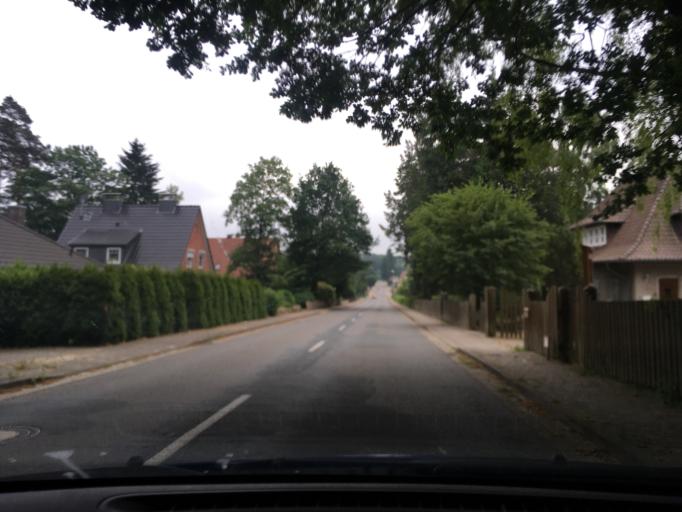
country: DE
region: Lower Saxony
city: Zernien
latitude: 53.0722
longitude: 10.8839
